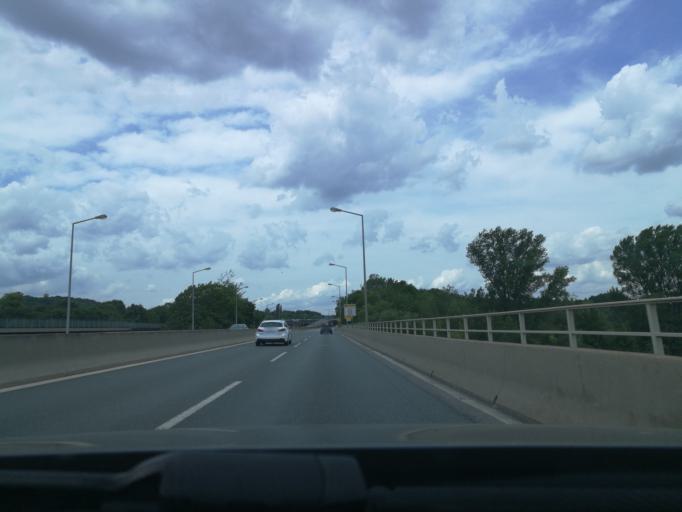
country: DE
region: Bavaria
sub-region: Regierungsbezirk Mittelfranken
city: Furth
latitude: 49.4541
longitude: 10.9834
